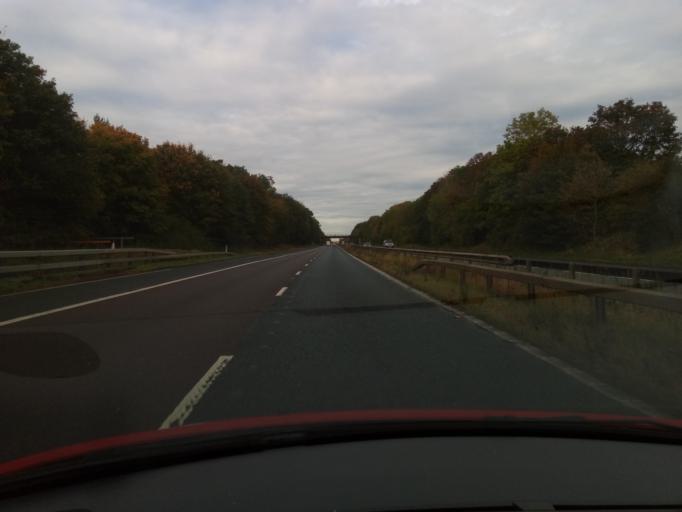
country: GB
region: England
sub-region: Darlington
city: High Coniscliffe
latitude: 54.5204
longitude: -1.6214
